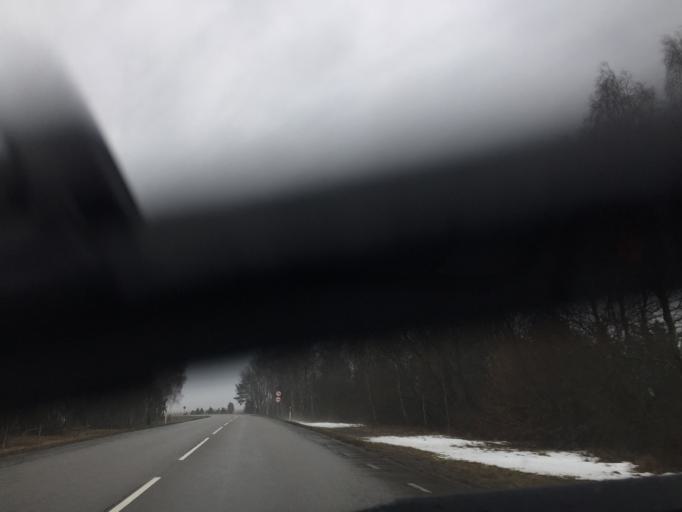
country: EE
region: Saare
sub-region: Orissaare vald
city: Orissaare
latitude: 58.5491
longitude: 23.1215
